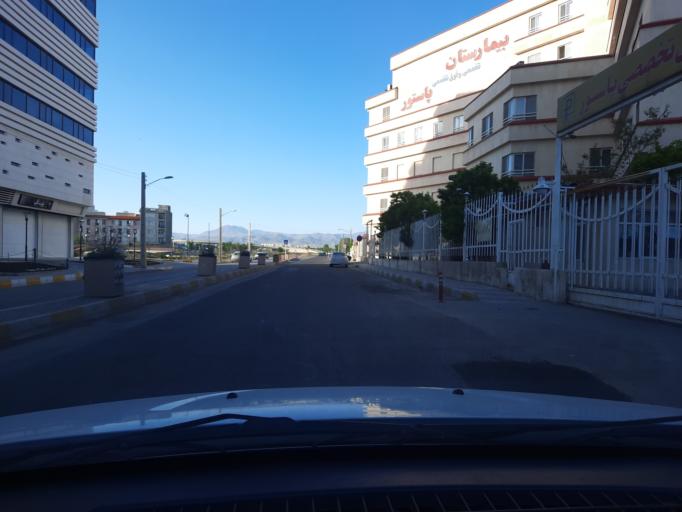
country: IR
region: Qazvin
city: Qazvin
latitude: 36.2664
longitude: 50.0244
